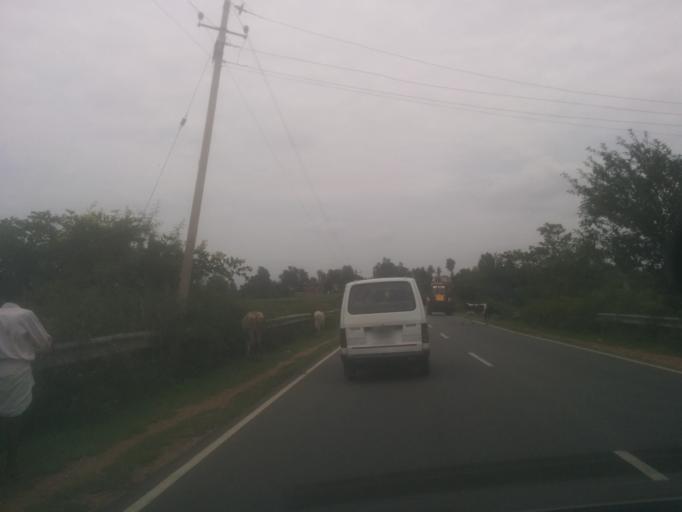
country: IN
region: Karnataka
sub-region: Hassan
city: Belur
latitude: 13.1634
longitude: 75.8880
